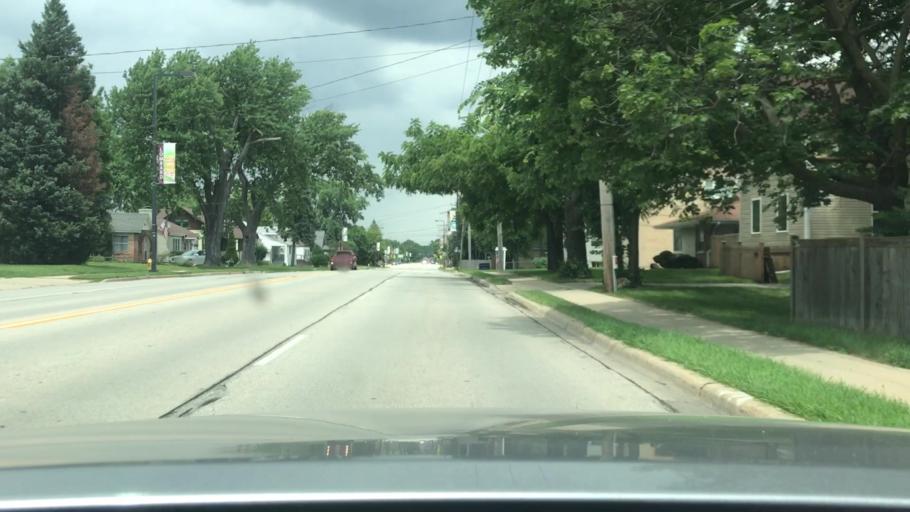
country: US
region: Illinois
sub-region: DuPage County
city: Villa Park
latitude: 41.8789
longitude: -87.9935
